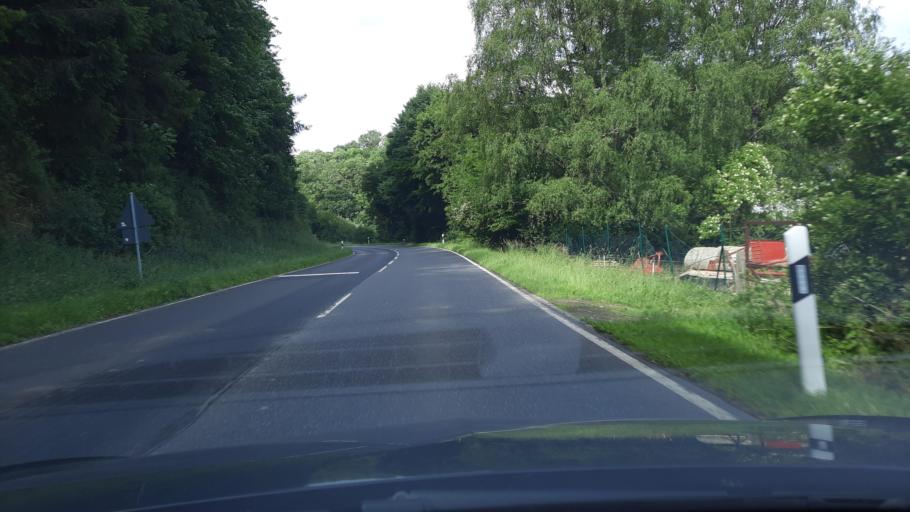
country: DE
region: Rheinland-Pfalz
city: Kempenich
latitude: 50.4169
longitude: 7.1205
